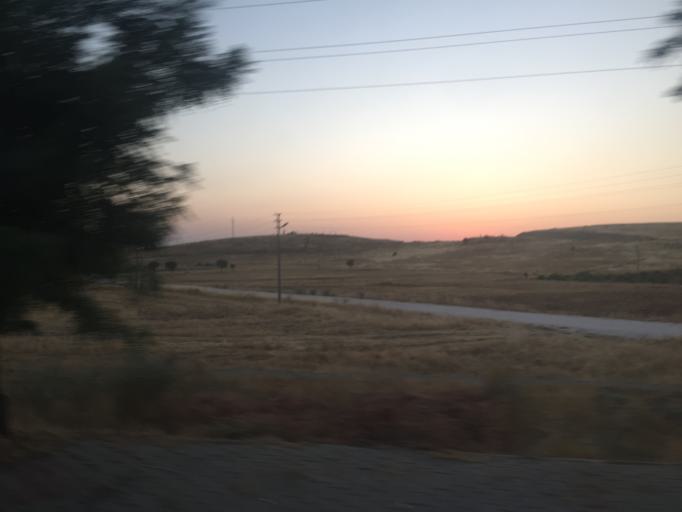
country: TR
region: Mardin
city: Kindirip
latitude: 37.4622
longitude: 41.2258
